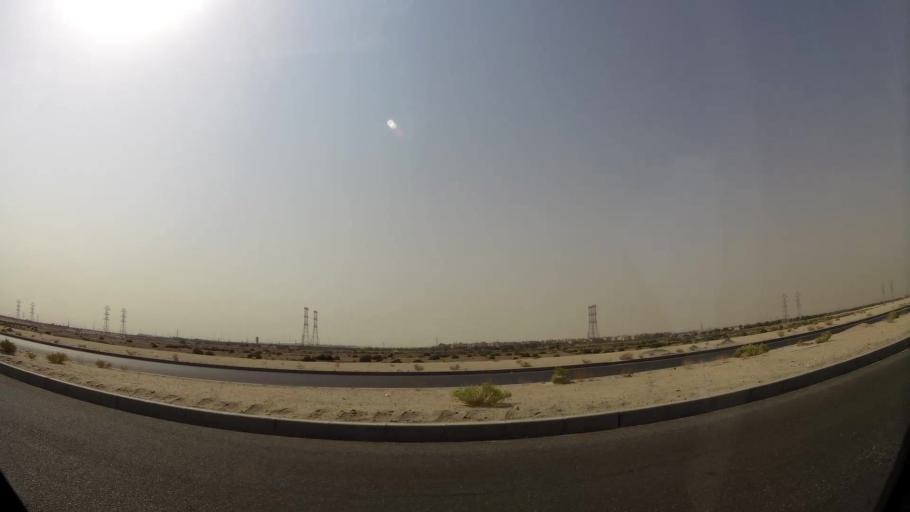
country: KW
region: Muhafazat al Jahra'
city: Al Jahra'
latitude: 29.3364
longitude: 47.7512
